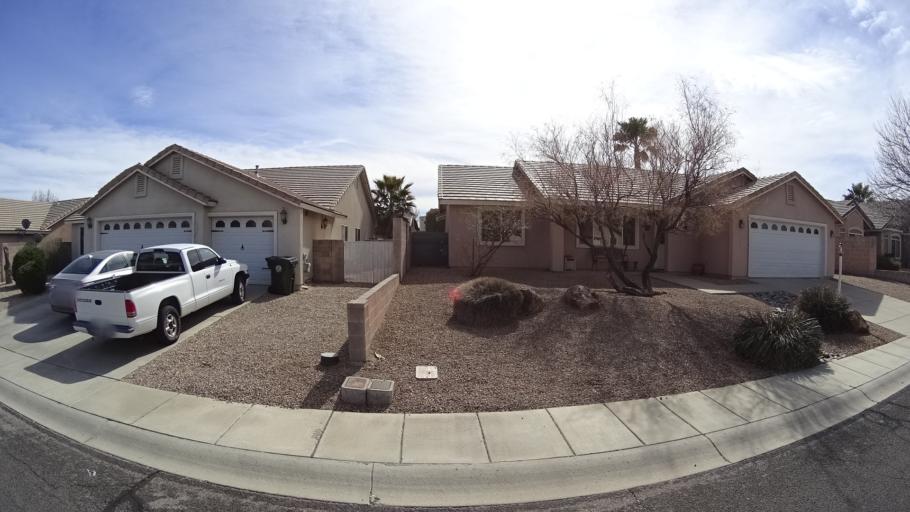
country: US
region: Arizona
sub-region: Mohave County
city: New Kingman-Butler
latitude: 35.2353
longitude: -114.0325
